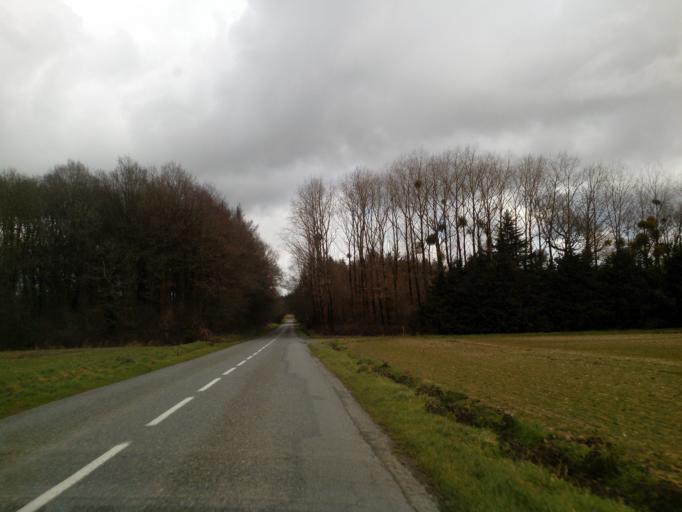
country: FR
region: Brittany
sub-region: Departement des Cotes-d'Armor
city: Sevignac
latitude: 48.2792
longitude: -2.3263
